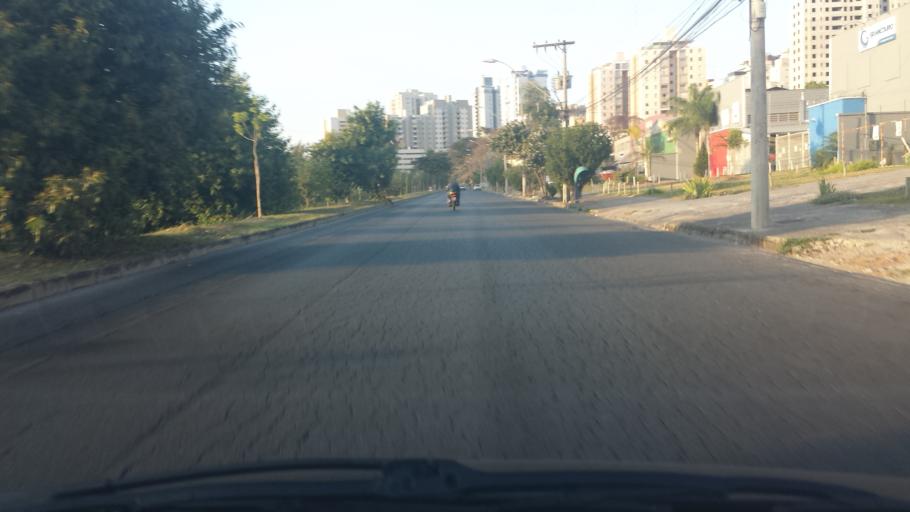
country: BR
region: Minas Gerais
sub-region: Belo Horizonte
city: Belo Horizonte
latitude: -19.8836
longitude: -43.9935
